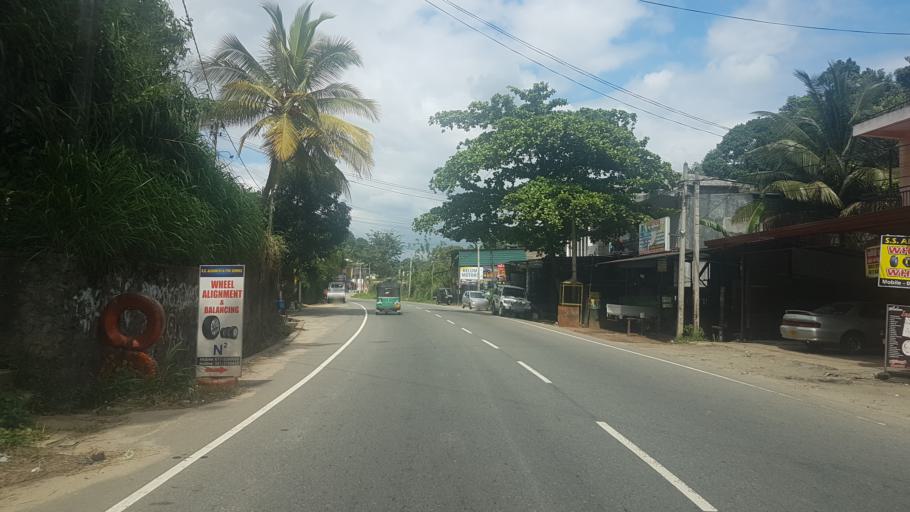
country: LK
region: Central
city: Gampola
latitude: 7.2069
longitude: 80.5991
